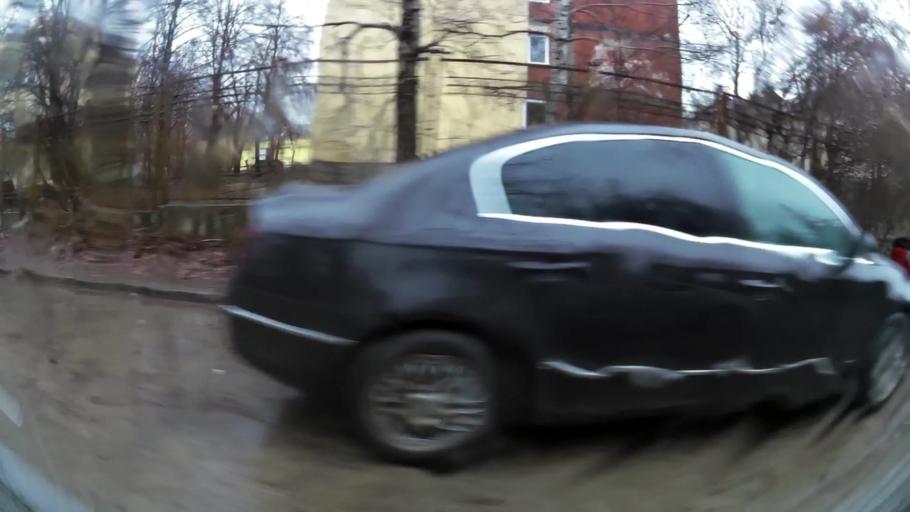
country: BG
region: Sofia-Capital
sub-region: Stolichna Obshtina
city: Sofia
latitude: 42.6499
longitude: 23.3386
